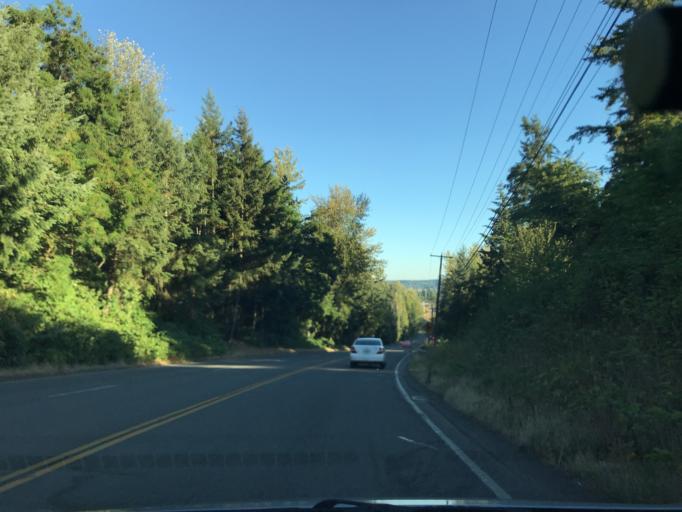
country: US
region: Washington
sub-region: Pierce County
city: Sumner
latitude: 47.2046
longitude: -122.2081
